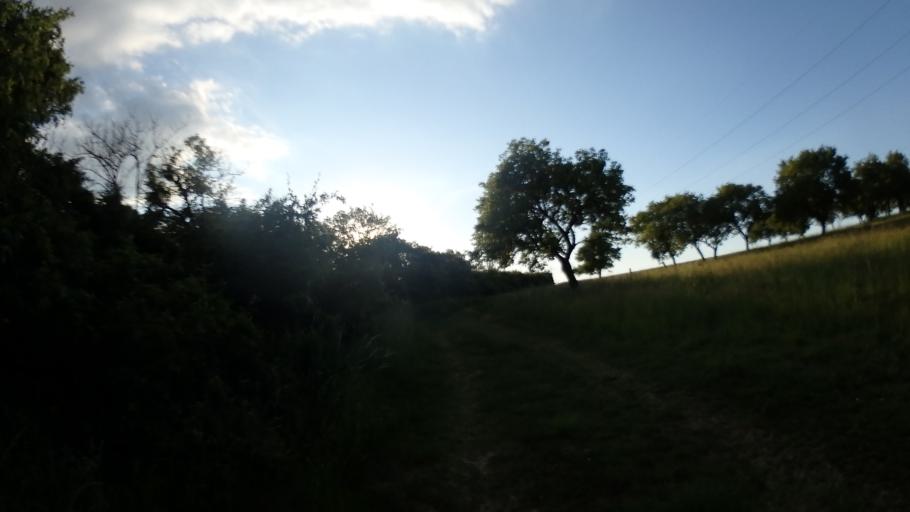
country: CZ
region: South Moravian
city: Zelesice
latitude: 49.1269
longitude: 16.5827
